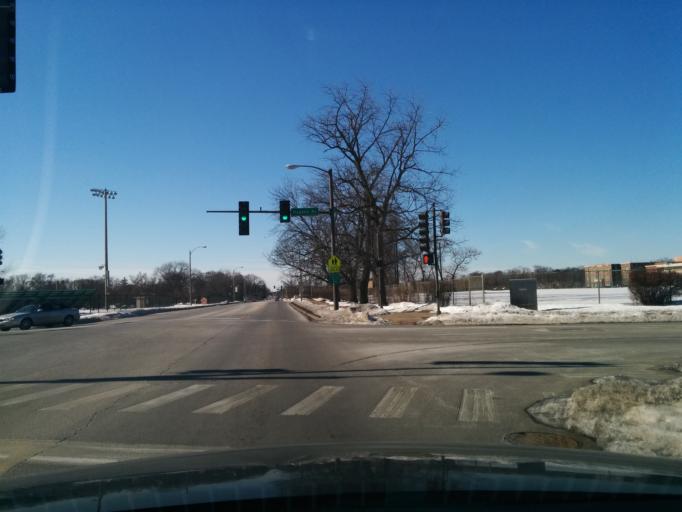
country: US
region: Illinois
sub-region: DuPage County
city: Elmhurst
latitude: 41.8904
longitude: -87.9493
